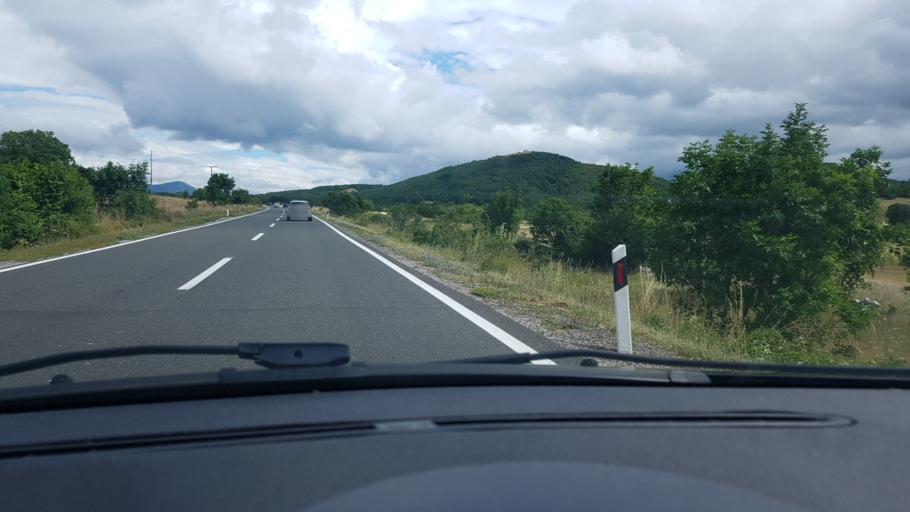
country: HR
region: Zadarska
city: Gracac
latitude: 44.4641
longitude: 15.8041
